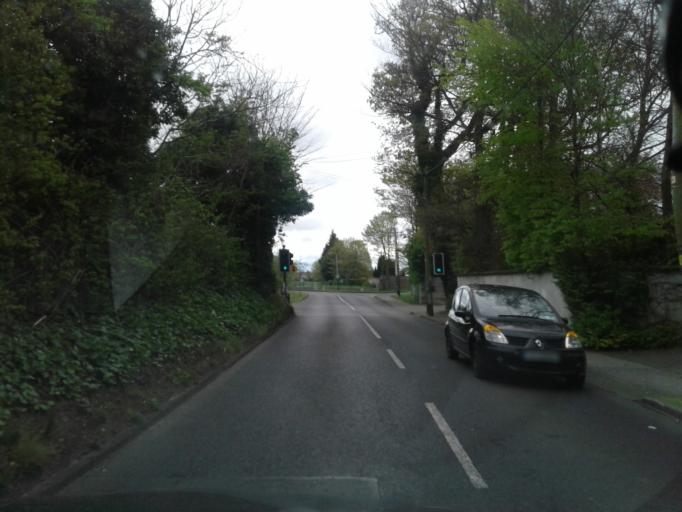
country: IE
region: Leinster
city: Ballyboden
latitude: 53.2822
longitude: -6.3171
